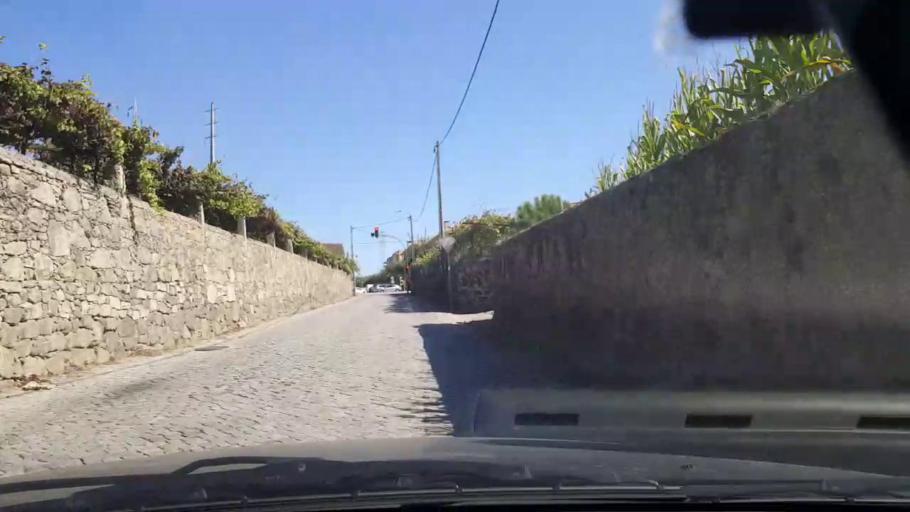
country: PT
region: Porto
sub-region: Vila do Conde
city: Arvore
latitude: 41.3111
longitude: -8.6804
